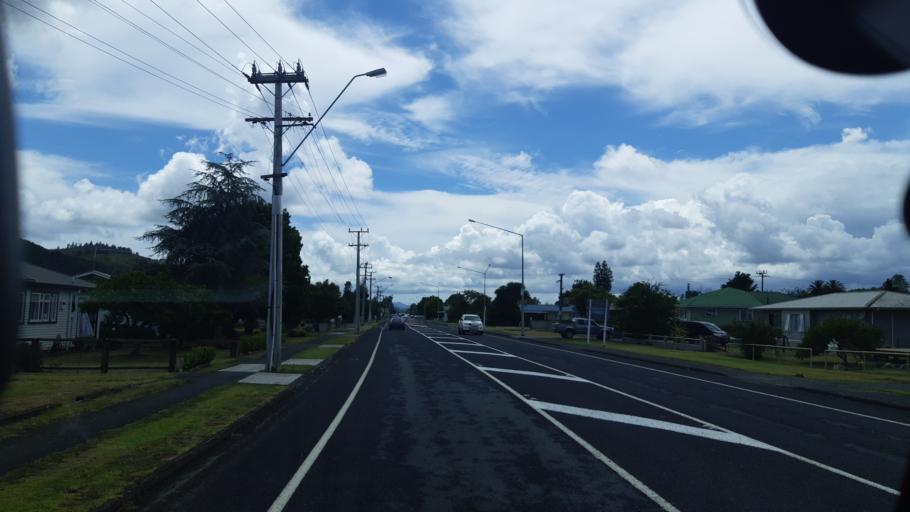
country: NZ
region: Northland
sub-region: Far North District
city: Moerewa
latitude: -35.3893
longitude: 174.0099
